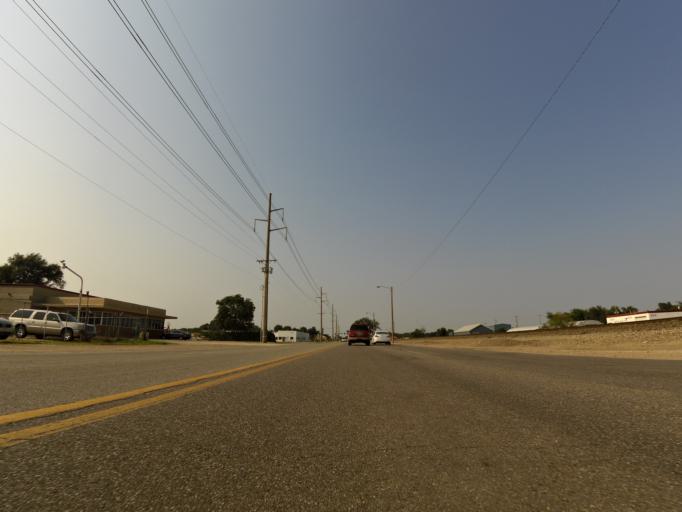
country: US
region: Kansas
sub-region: Sedgwick County
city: Park City
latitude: 37.7495
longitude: -97.3360
